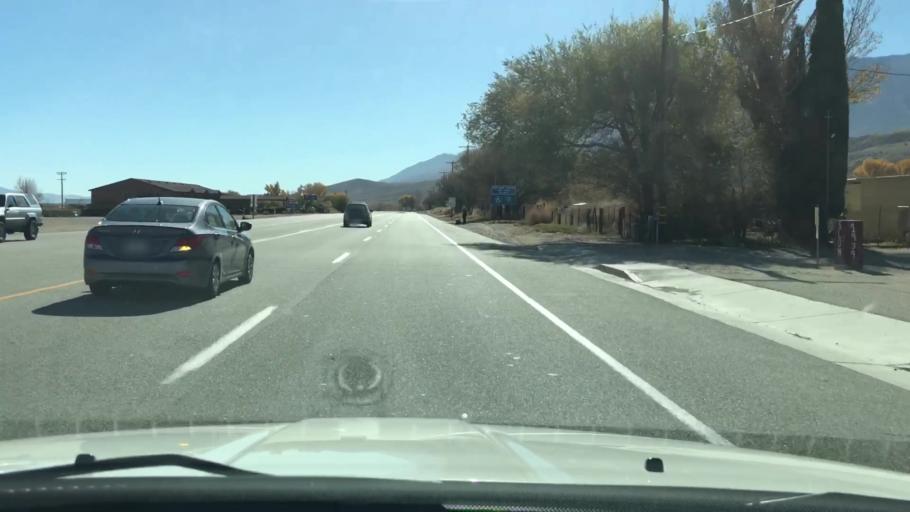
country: US
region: California
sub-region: Inyo County
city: Lone Pine
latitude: 36.5831
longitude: -118.0577
